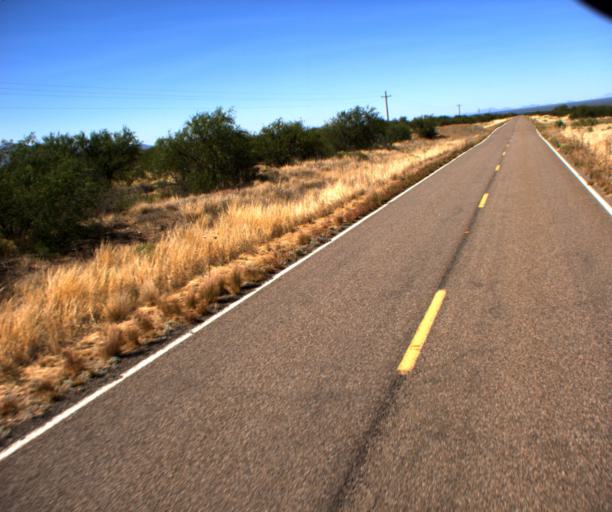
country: US
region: Arizona
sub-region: Pima County
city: Three Points
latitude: 31.7782
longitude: -111.4626
